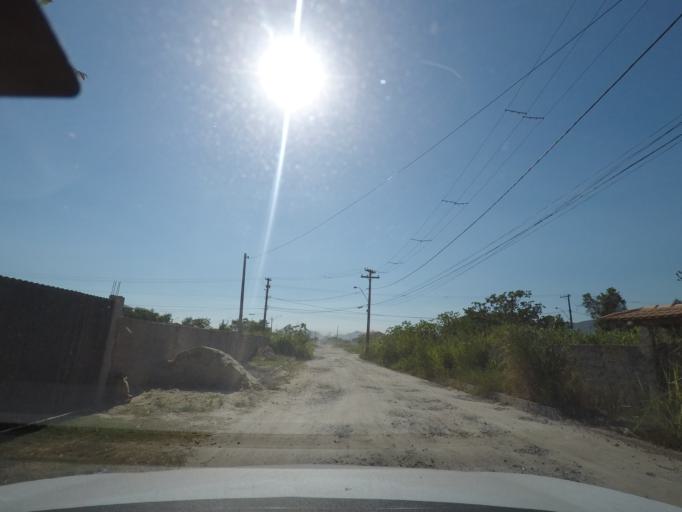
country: BR
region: Rio de Janeiro
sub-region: Marica
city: Marica
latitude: -22.9644
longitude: -42.9257
